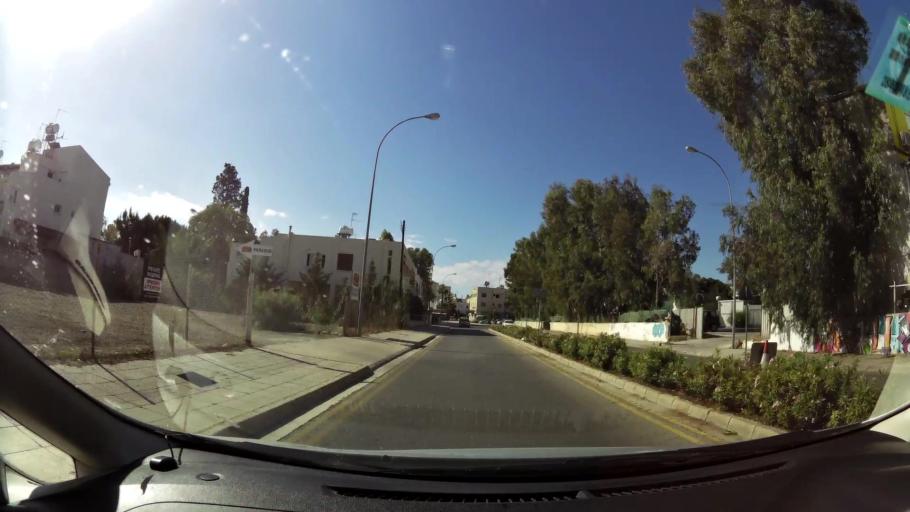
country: CY
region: Lefkosia
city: Nicosia
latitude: 35.1399
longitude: 33.3370
